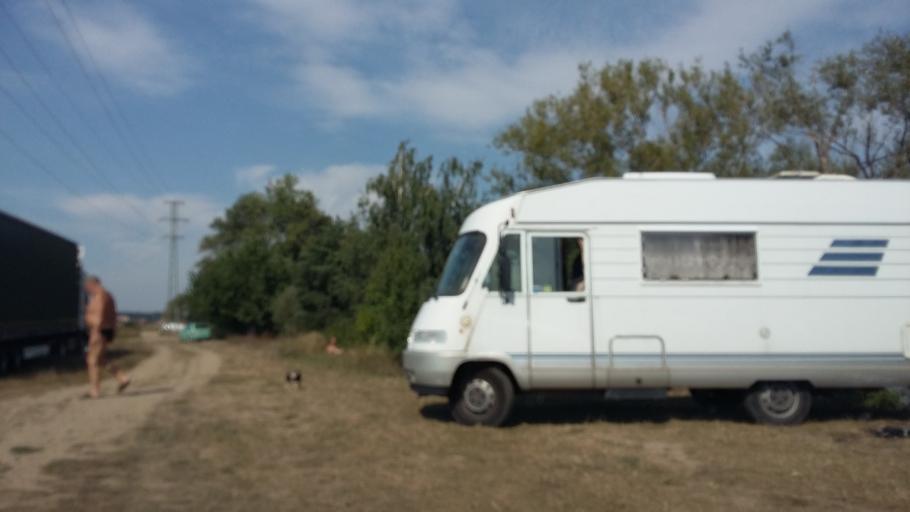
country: CZ
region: Central Bohemia
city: Veltruby
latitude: 50.0825
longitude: 15.1877
